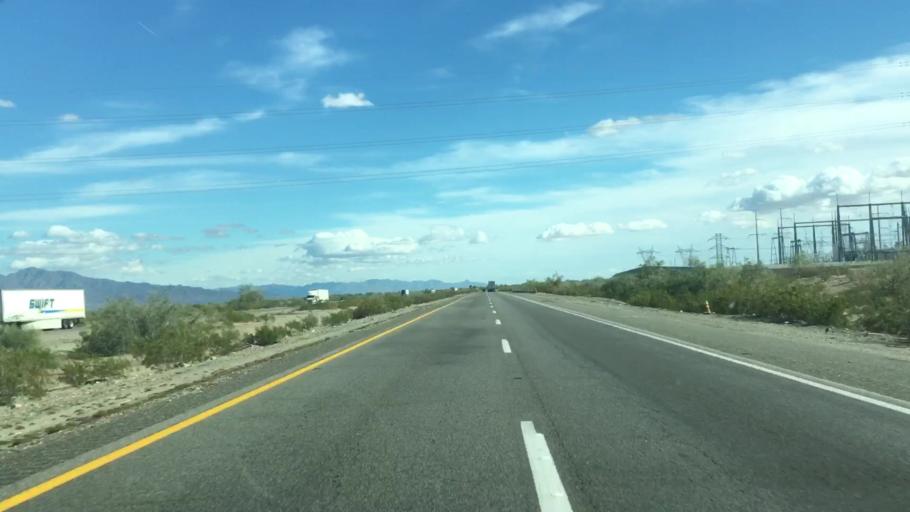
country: US
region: California
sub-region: Imperial County
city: Niland
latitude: 33.7027
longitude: -115.3186
